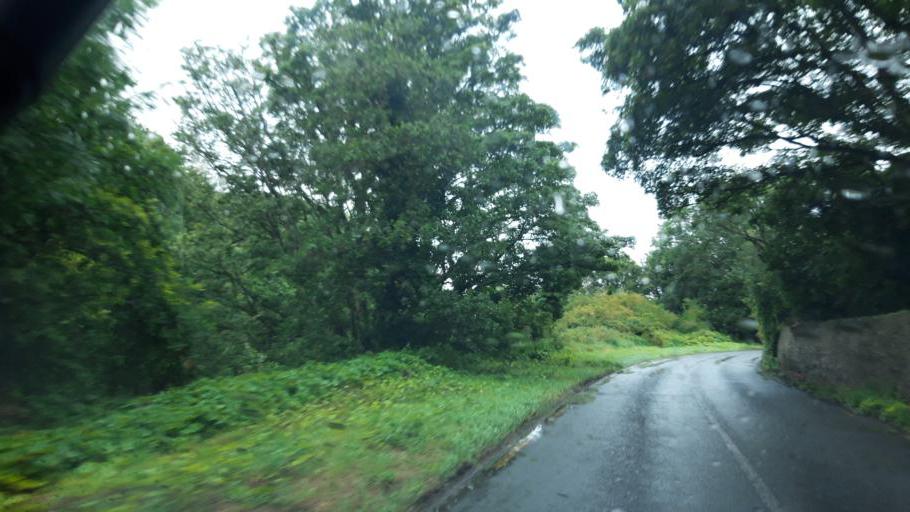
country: IE
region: Leinster
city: Hartstown
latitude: 53.3680
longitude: -6.4172
